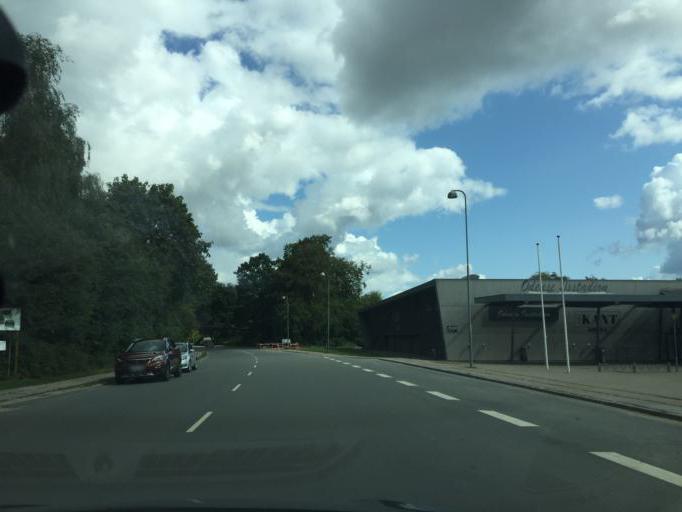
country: DK
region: South Denmark
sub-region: Odense Kommune
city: Odense
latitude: 55.4000
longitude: 10.3488
